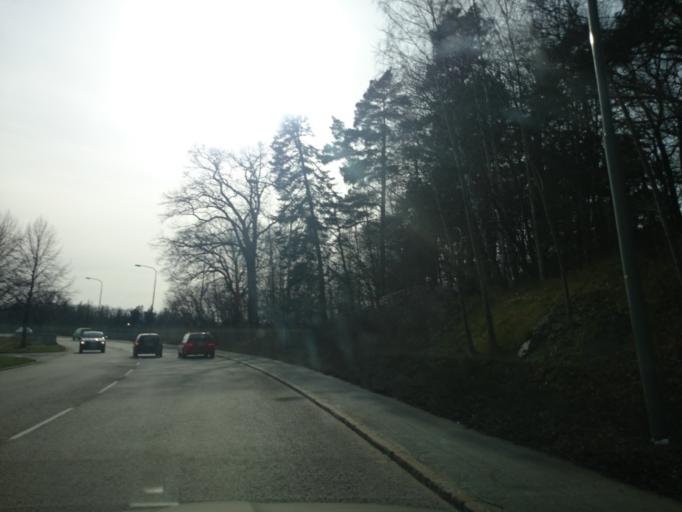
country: SE
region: Stockholm
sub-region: Stockholms Kommun
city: Arsta
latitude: 59.2338
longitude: 18.0907
